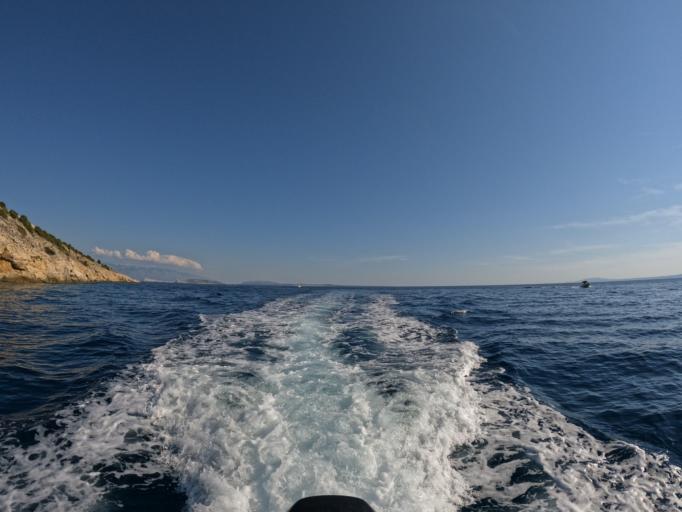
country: HR
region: Primorsko-Goranska
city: Punat
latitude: 44.9659
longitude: 14.6478
